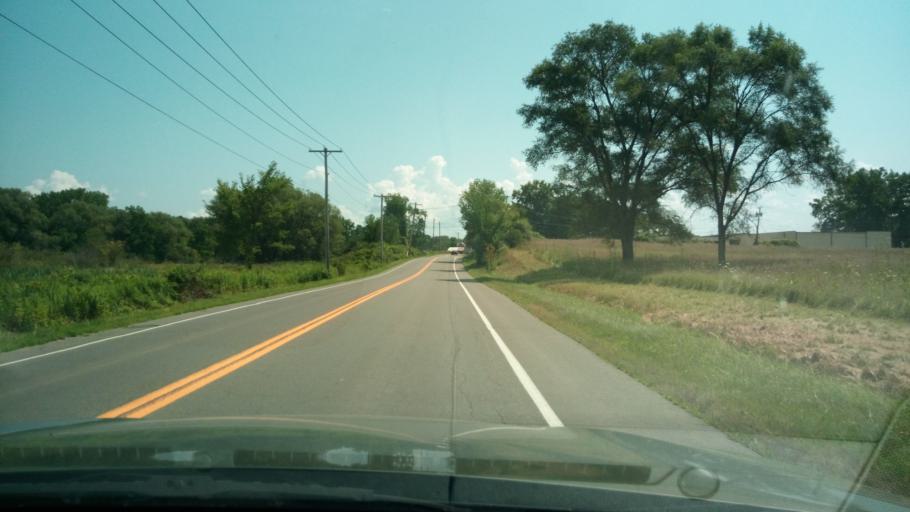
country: US
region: New York
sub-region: Chemung County
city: Horseheads North
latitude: 42.1899
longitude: -76.8295
